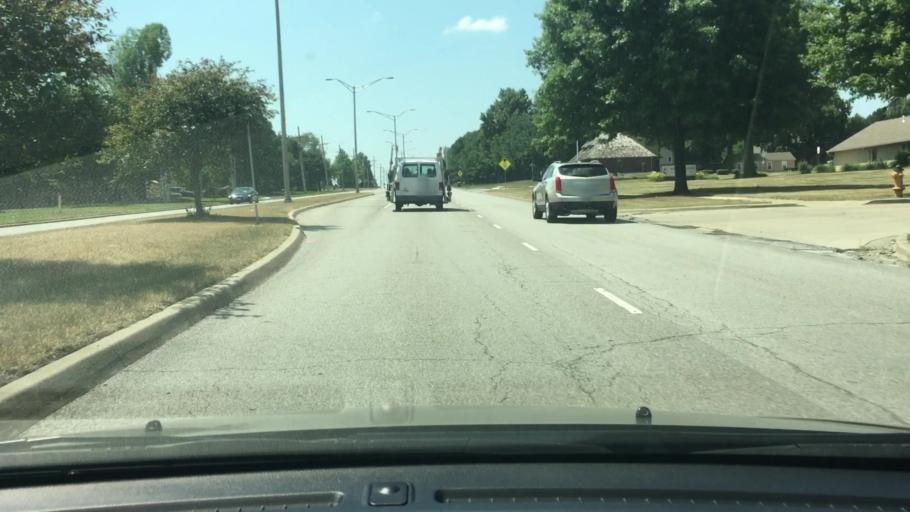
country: US
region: Kansas
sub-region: Johnson County
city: Lenexa
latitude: 38.8946
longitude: -94.7238
